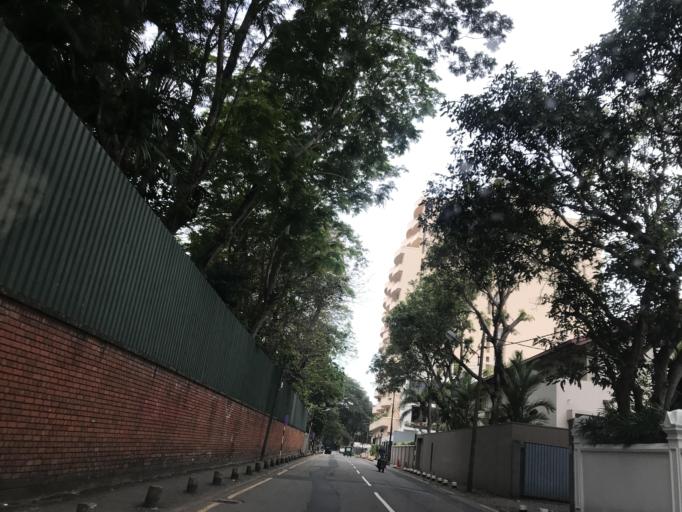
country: LK
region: Western
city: Colombo
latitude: 6.8992
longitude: 79.8574
